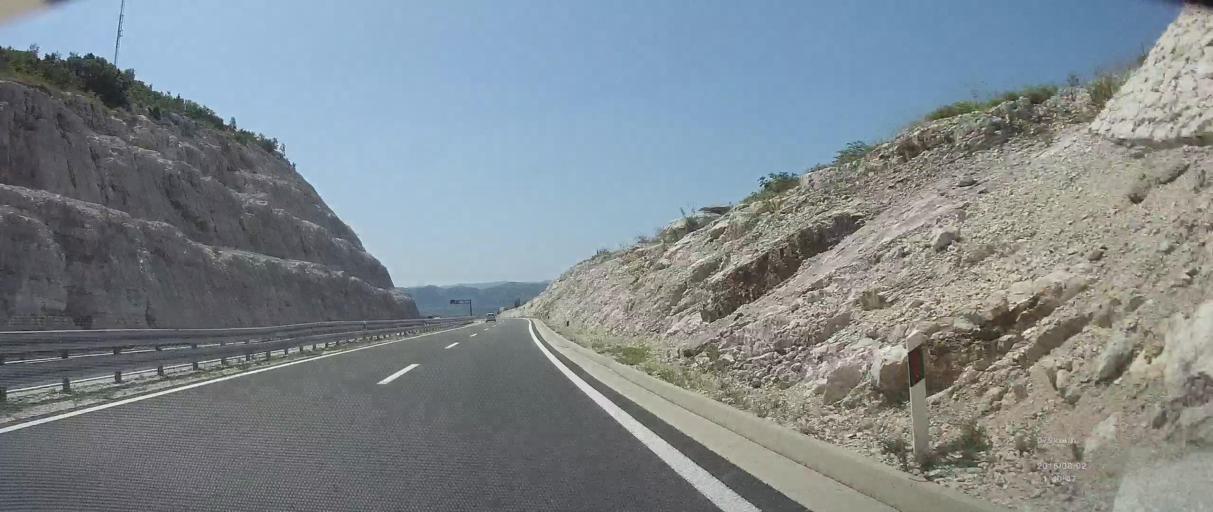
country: HR
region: Dubrovacko-Neretvanska
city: Komin
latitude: 43.0710
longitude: 17.4932
